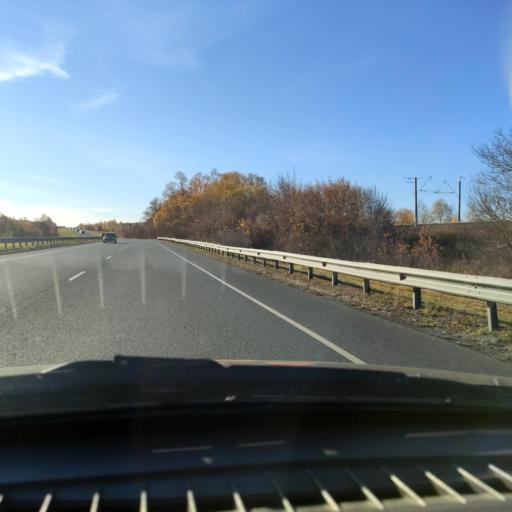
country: RU
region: Samara
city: Mezhdurechensk
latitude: 53.2441
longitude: 48.9858
